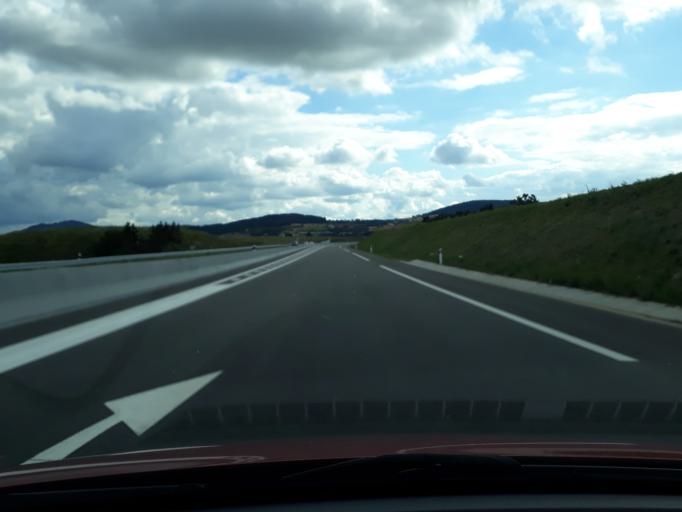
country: FR
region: Auvergne
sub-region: Departement de la Haute-Loire
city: Cussac-sur-Loire
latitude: 45.0045
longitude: 3.8815
